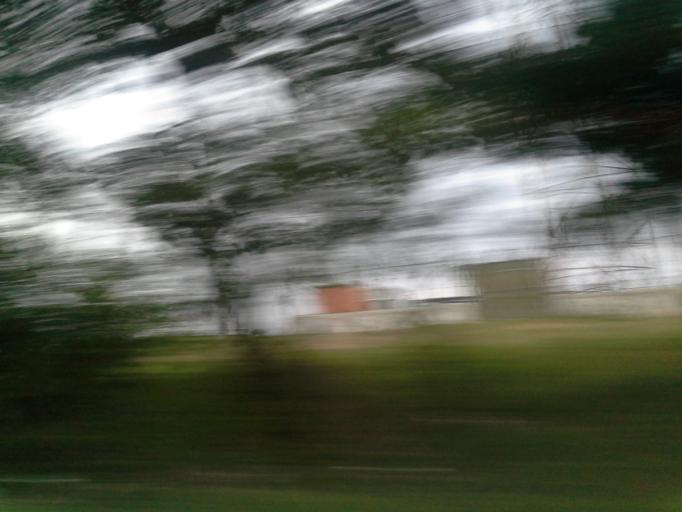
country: CO
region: Sucre
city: Los Palmitos
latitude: 9.3702
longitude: -75.2725
